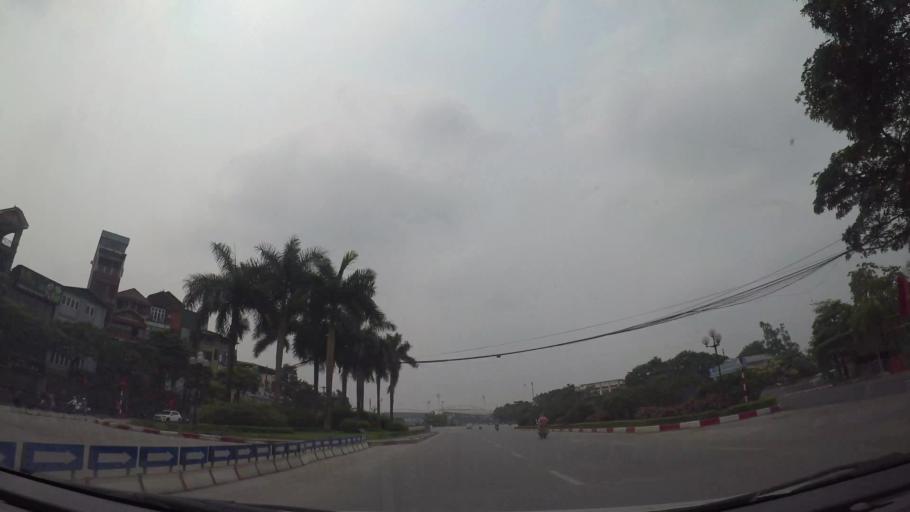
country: VN
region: Ha Noi
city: Cau Dien
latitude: 21.0143
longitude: 105.7696
